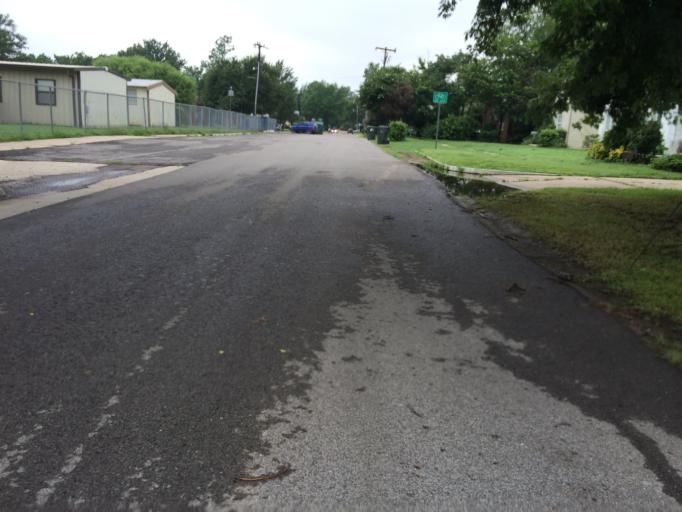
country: US
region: Oklahoma
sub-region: Cleveland County
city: Norman
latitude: 35.2154
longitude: -97.4349
